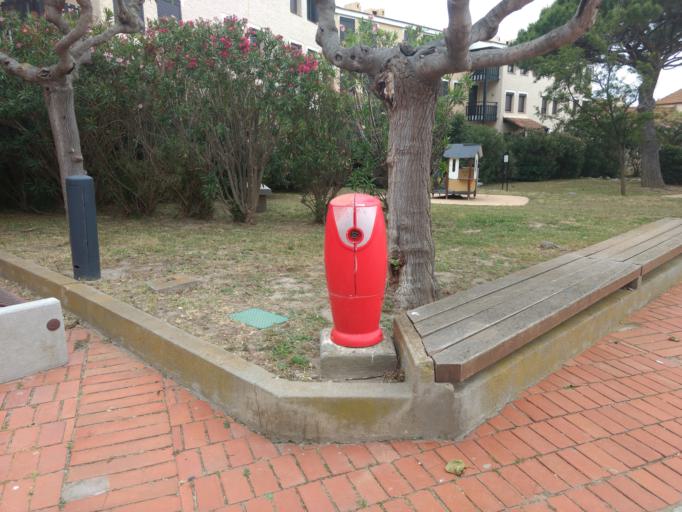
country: FR
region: Languedoc-Roussillon
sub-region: Departement des Pyrenees-Orientales
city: Le Barcares
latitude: 42.8147
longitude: 3.0214
